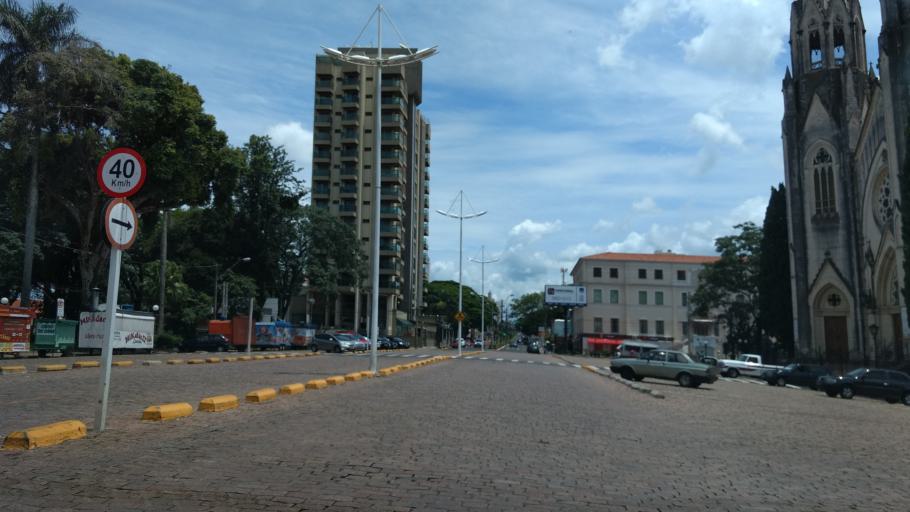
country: BR
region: Sao Paulo
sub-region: Botucatu
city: Botucatu
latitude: -22.8855
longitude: -48.4445
